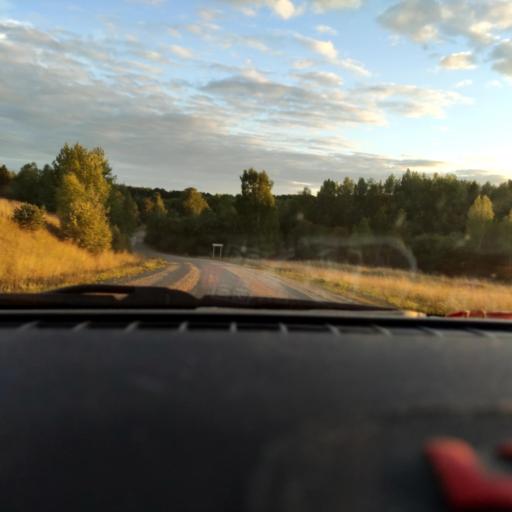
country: RU
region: Perm
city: Ocher
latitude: 57.9563
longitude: 54.8113
